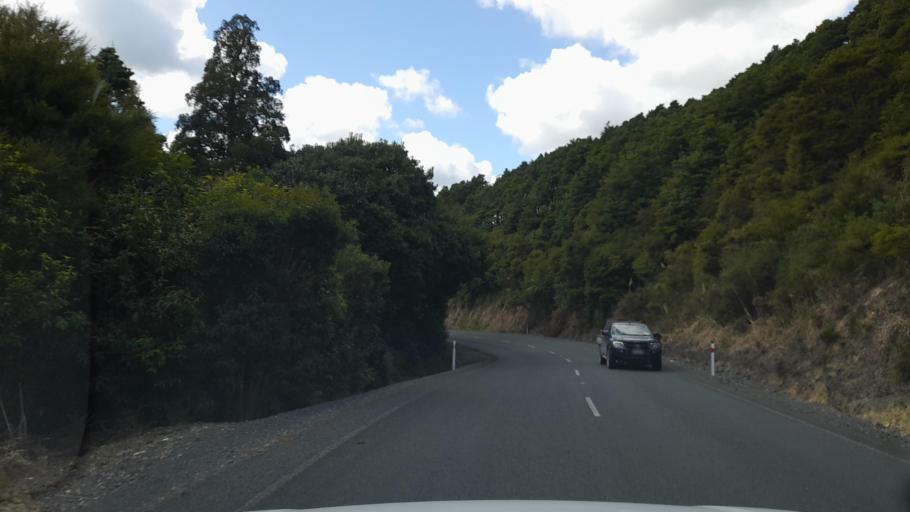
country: NZ
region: Northland
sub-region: Whangarei
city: Maungatapere
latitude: -35.7005
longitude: 174.0463
